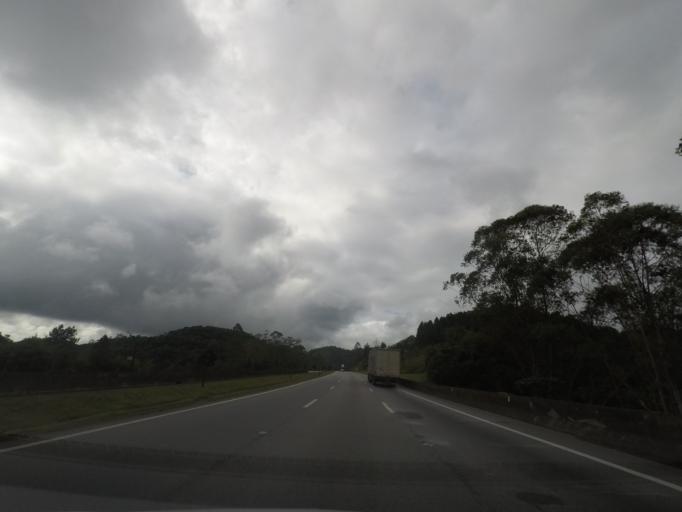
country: BR
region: Sao Paulo
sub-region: Juquitiba
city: Juquitiba
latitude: -24.0012
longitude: -47.1512
